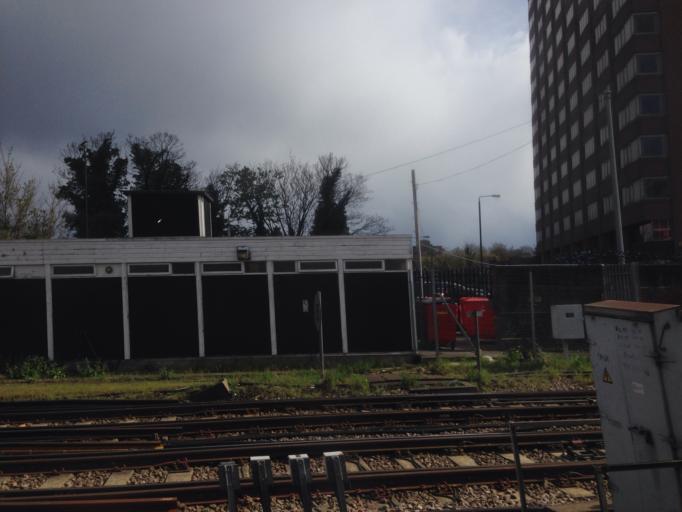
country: GB
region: England
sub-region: Greater London
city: Sutton
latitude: 51.3599
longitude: -0.1898
